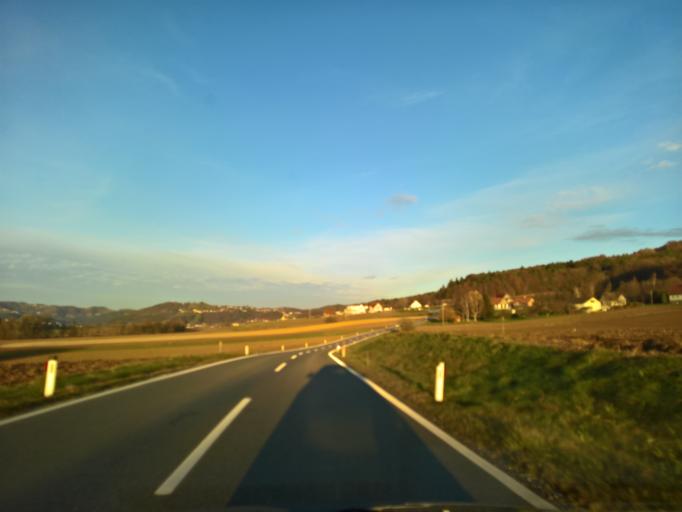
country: AT
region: Styria
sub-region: Politischer Bezirk Leibnitz
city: Sankt Johann im Saggautal
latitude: 46.7217
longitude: 15.4142
